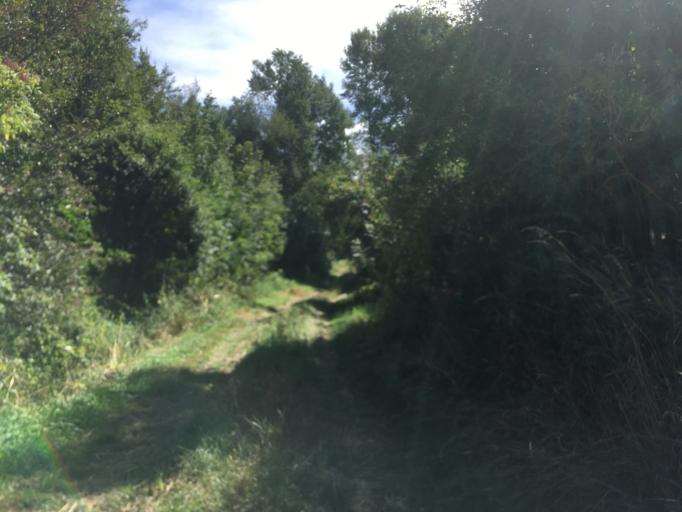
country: DE
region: Brandenburg
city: Gerswalde
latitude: 53.1306
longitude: 13.7859
